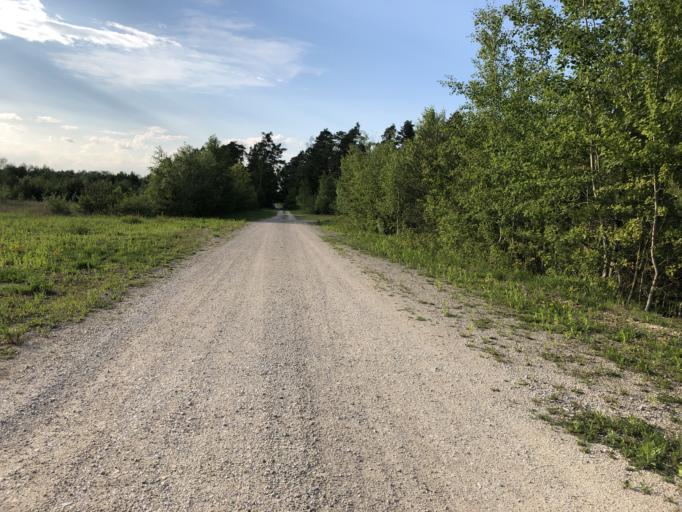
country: DE
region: Bavaria
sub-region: Upper Franconia
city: Memmelsdorf
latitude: 49.9089
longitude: 10.9482
